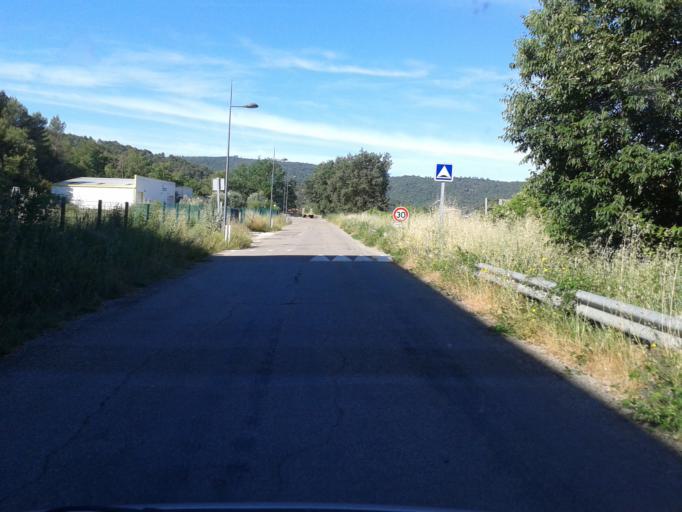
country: FR
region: Provence-Alpes-Cote d'Azur
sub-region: Departement du Vaucluse
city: Beaumont-de-Pertuis
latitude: 43.6950
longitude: 5.7298
